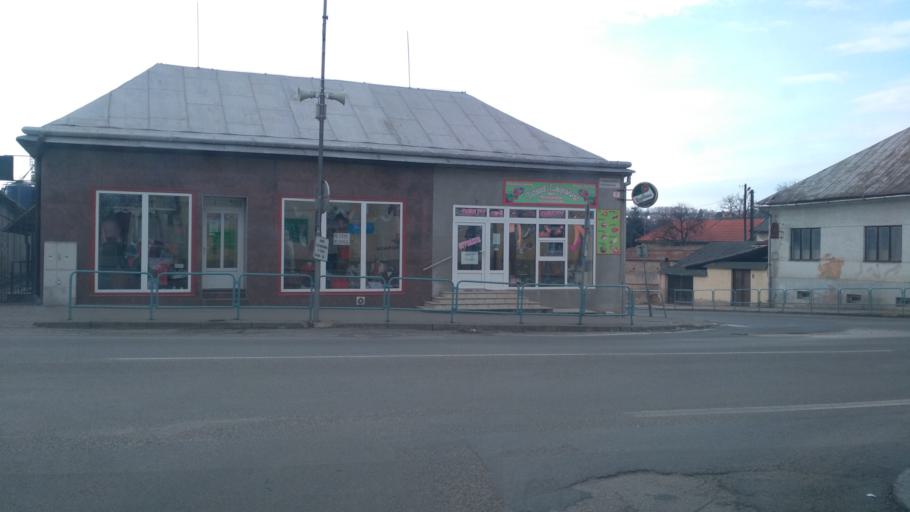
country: SK
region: Kosicky
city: Moldava nad Bodvou
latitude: 48.6101
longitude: 21.0011
